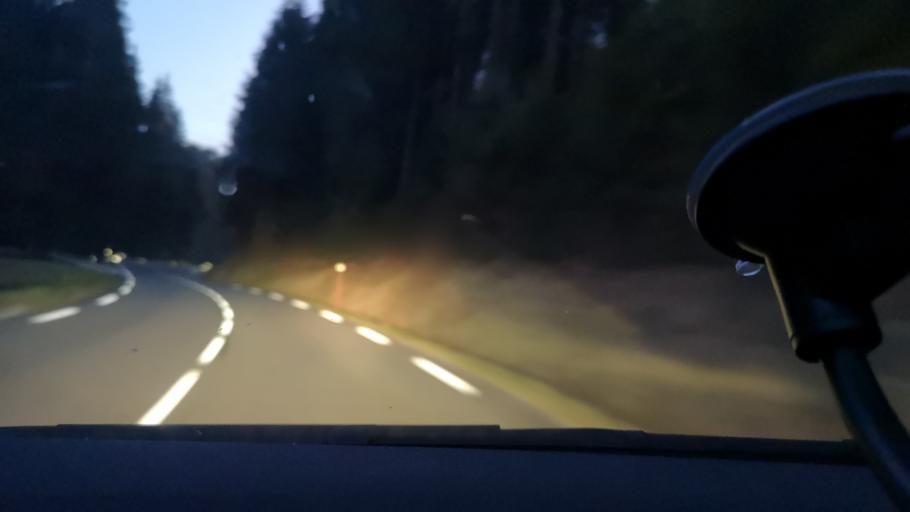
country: FR
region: Franche-Comte
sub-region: Departement du Jura
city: Champagnole
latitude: 46.7580
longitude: 5.9760
